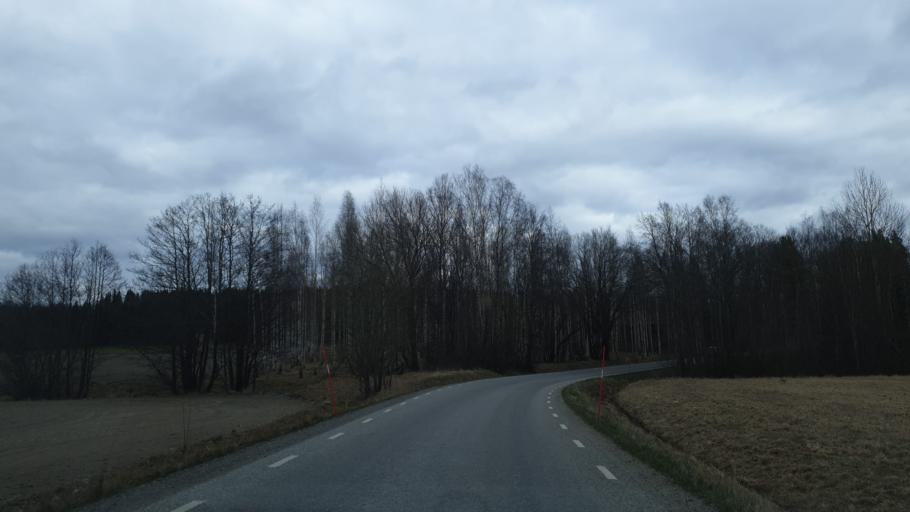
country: SE
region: OErebro
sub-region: Nora Kommun
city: As
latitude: 59.6113
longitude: 15.0035
